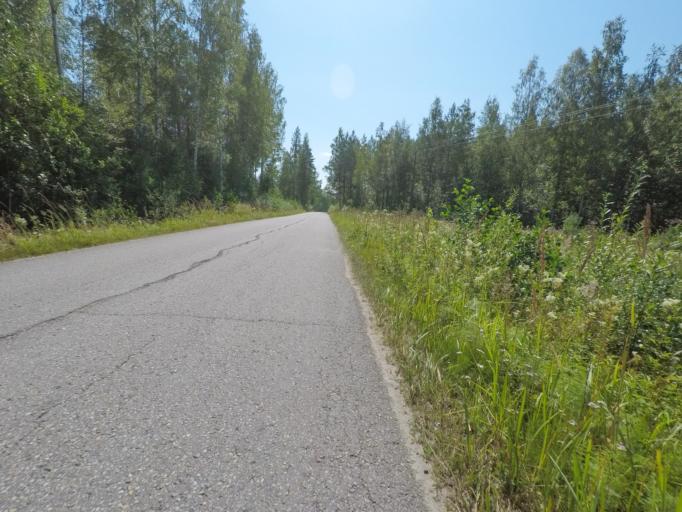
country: FI
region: Southern Savonia
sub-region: Mikkeli
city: Puumala
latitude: 61.4124
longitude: 28.0923
